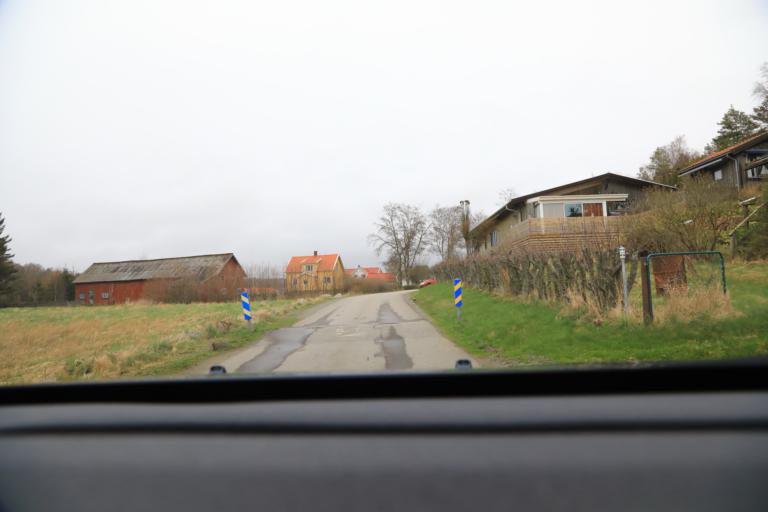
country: SE
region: Halland
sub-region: Kungsbacka Kommun
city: Frillesas
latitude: 57.2984
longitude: 12.1748
